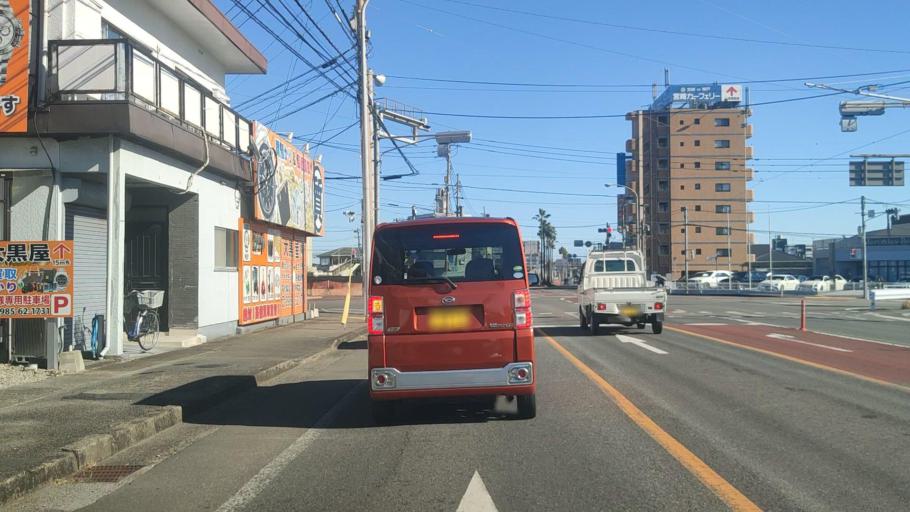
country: JP
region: Miyazaki
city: Miyazaki-shi
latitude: 31.9075
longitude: 131.4466
